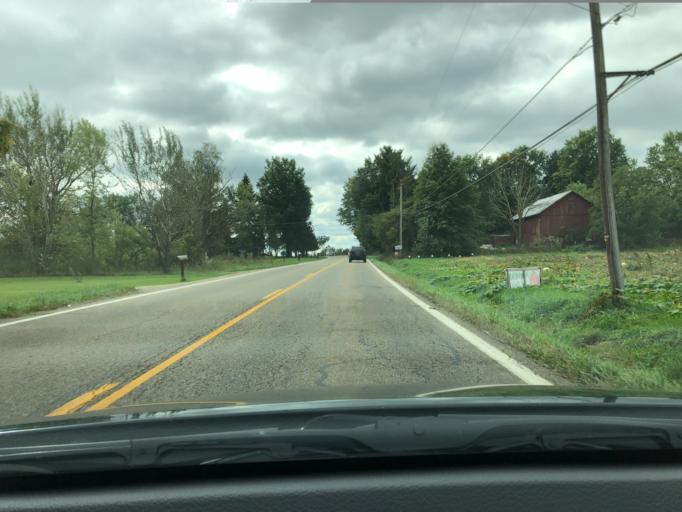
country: US
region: Ohio
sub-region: Stark County
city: Canal Fulton
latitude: 40.8251
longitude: -81.6005
